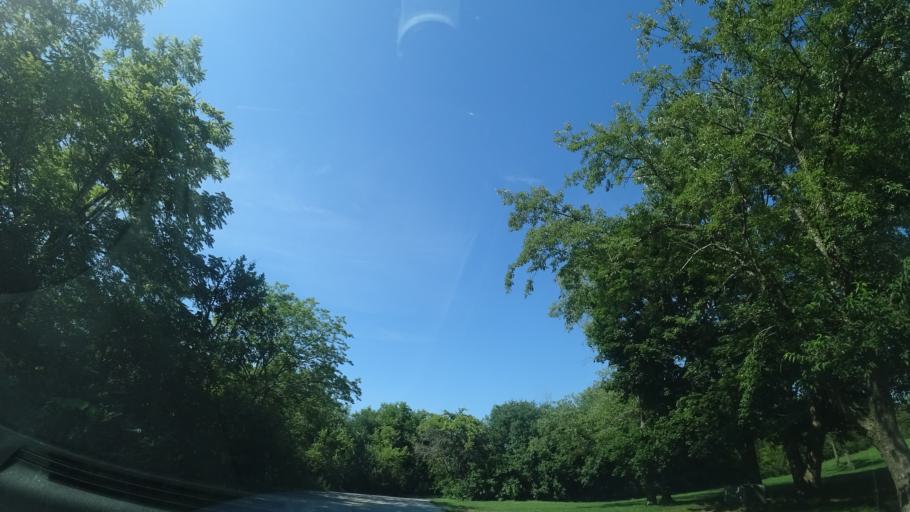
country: US
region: Illinois
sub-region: Cook County
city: Orland Hills
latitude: 41.5770
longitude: -87.8871
